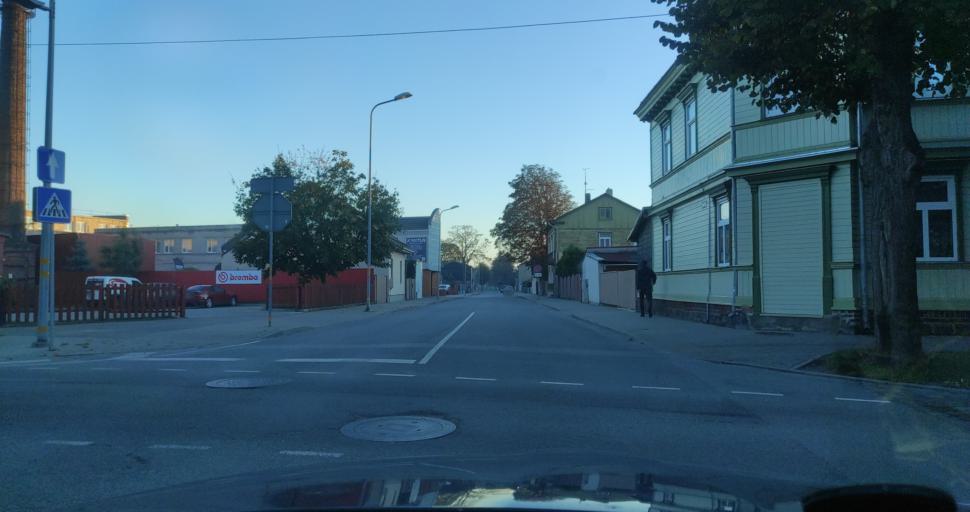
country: LV
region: Liepaja
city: Liepaja
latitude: 56.5010
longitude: 21.0120
